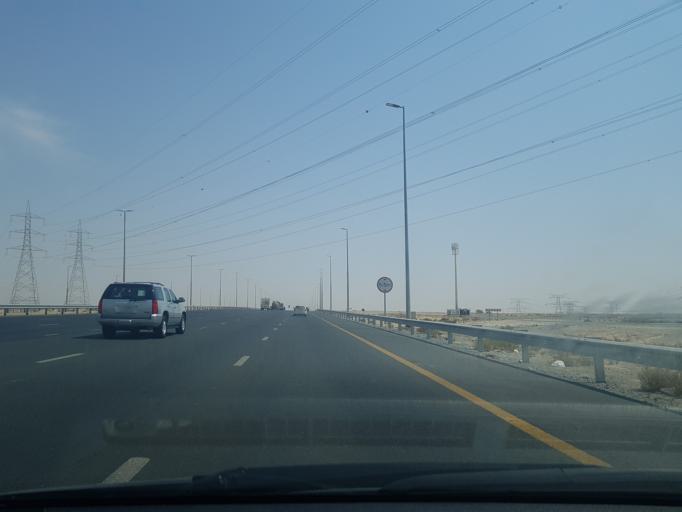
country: AE
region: Ash Shariqah
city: Sharjah
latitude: 25.2424
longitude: 55.5555
